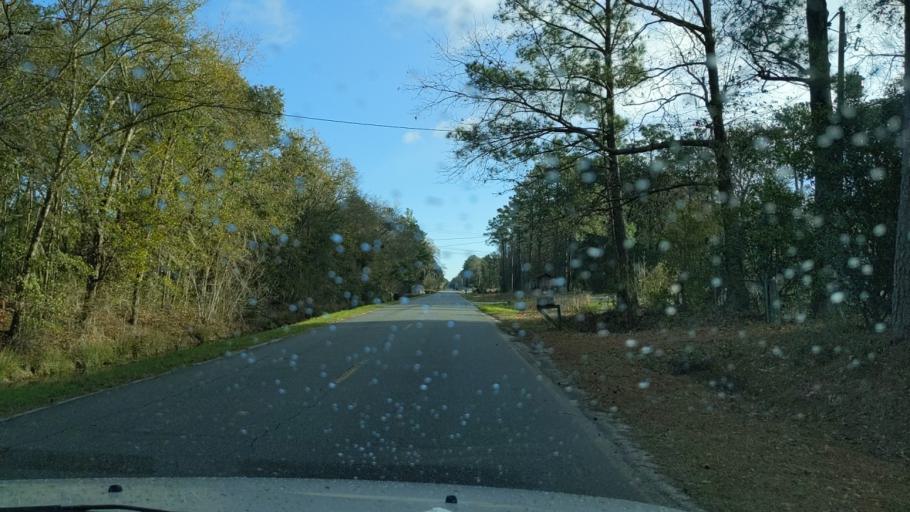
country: US
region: Georgia
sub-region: Chatham County
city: Georgetown
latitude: 32.0360
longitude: -81.3041
